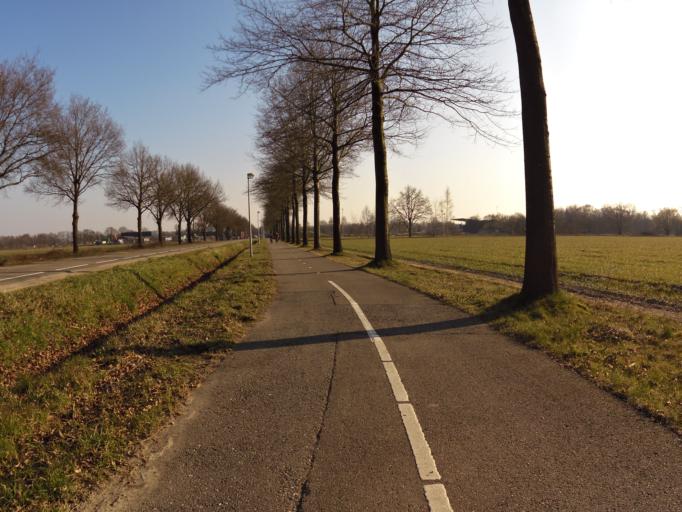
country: NL
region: North Brabant
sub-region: Gemeente Maasdonk
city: Geffen
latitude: 51.7143
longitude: 5.4332
